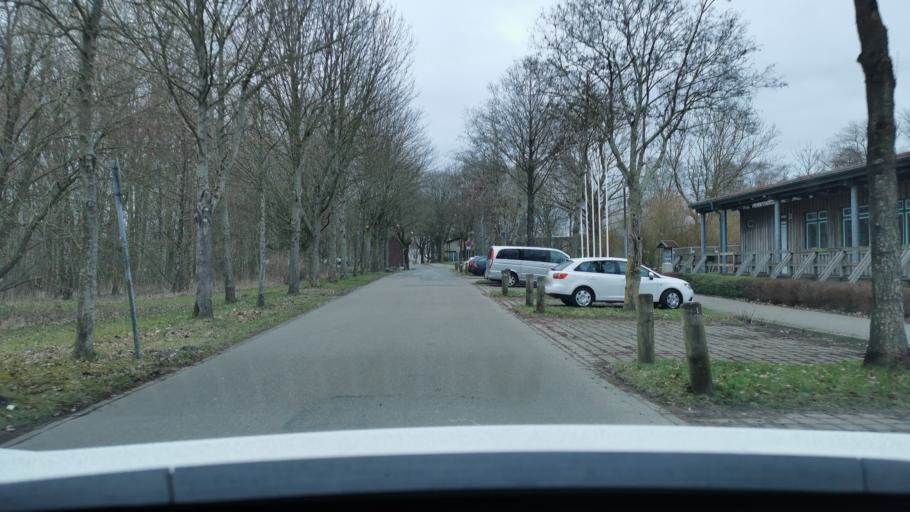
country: DE
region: Schleswig-Holstein
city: Rendsburg
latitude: 54.3042
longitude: 9.6555
